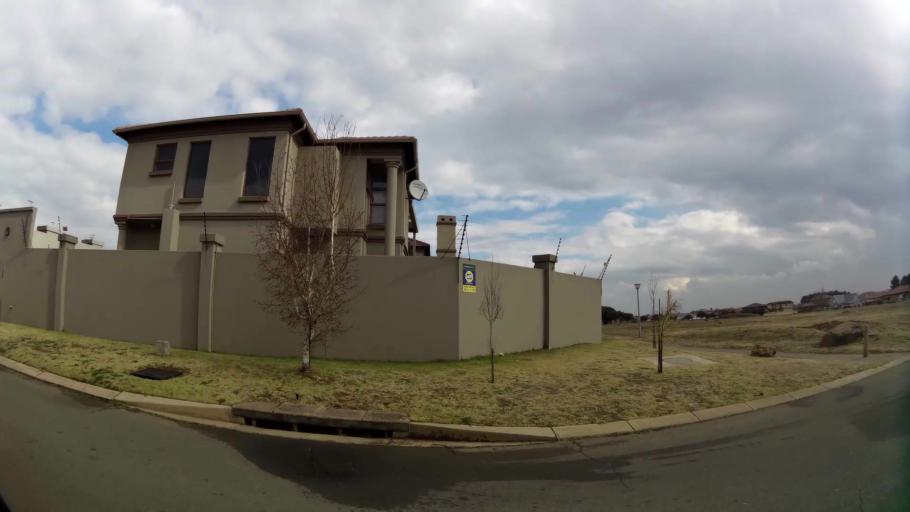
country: ZA
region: Gauteng
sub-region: Sedibeng District Municipality
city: Vanderbijlpark
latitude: -26.7255
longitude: 27.8680
